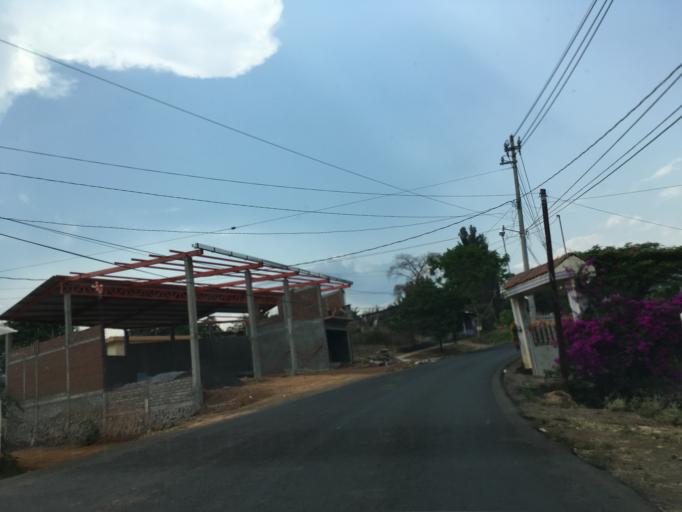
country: MX
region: Michoacan
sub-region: Ziracuaretiro
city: Patuan
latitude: 19.4176
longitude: -101.9188
